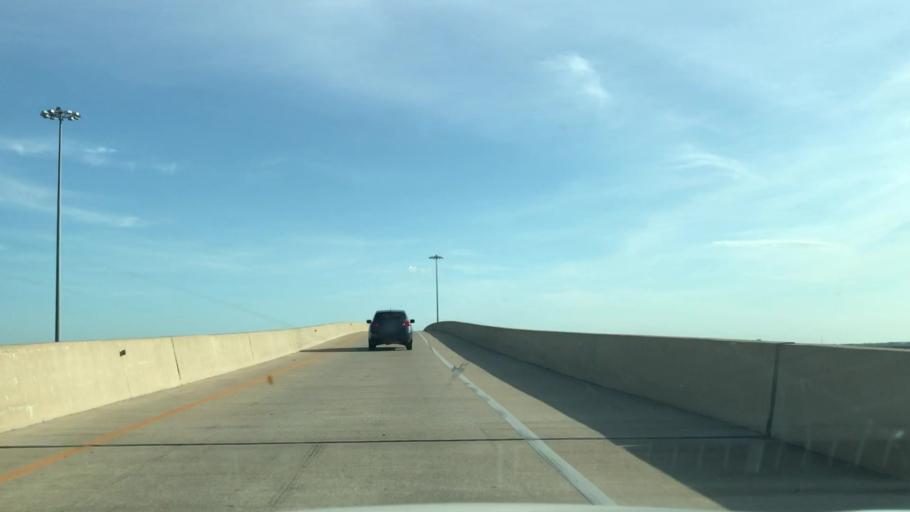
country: US
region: Texas
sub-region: Dallas County
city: Rowlett
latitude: 32.8589
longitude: -96.5556
